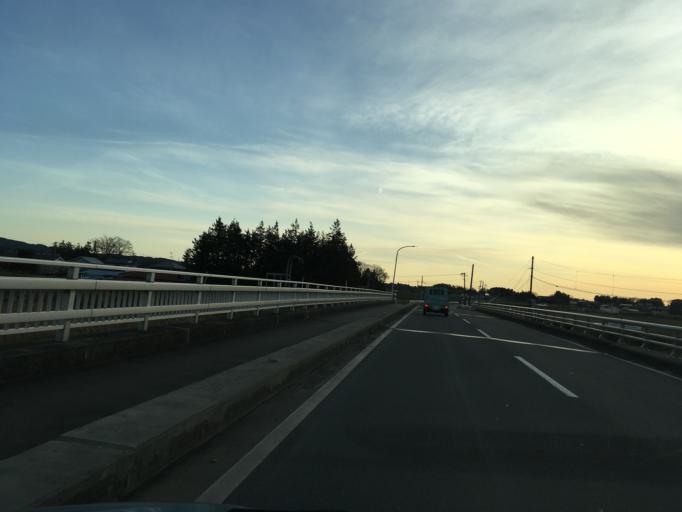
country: JP
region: Miyagi
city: Kogota
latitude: 38.6450
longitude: 141.0743
